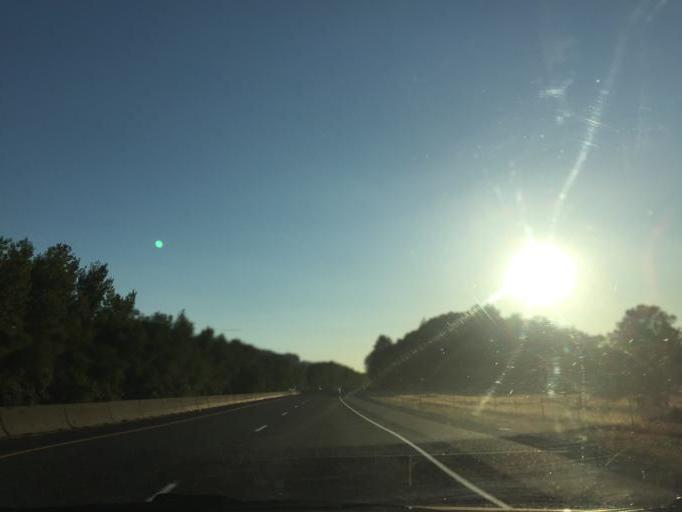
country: US
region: Washington
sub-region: Clark County
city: Washougal
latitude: 45.5491
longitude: -122.2006
